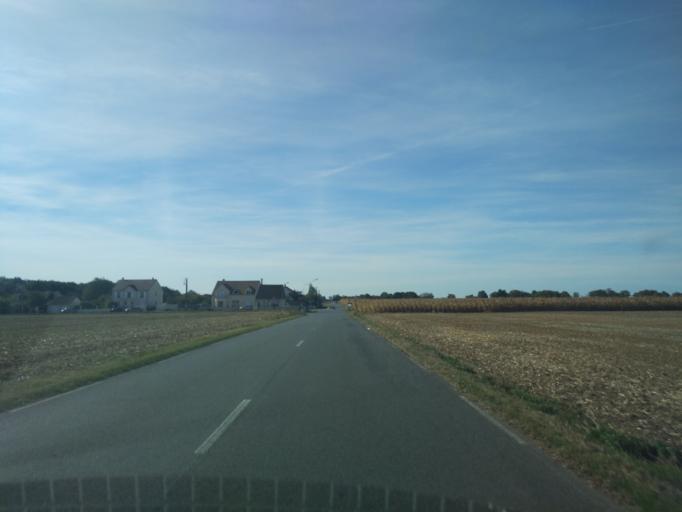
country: FR
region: Ile-de-France
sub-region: Departement de l'Essonne
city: Limours
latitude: 48.6530
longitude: 2.0879
